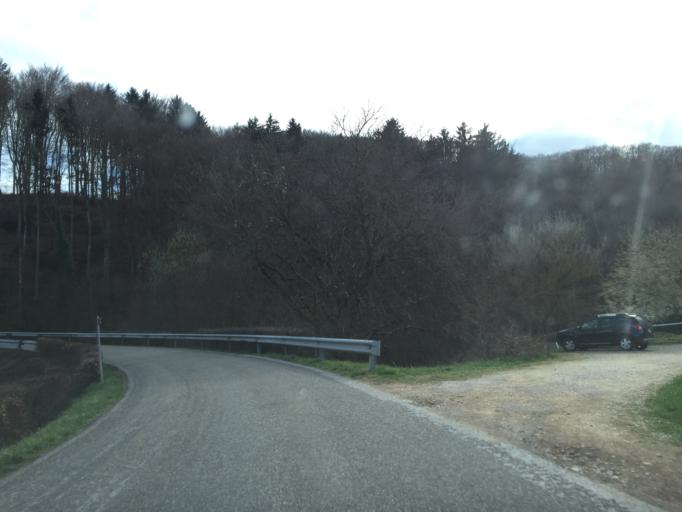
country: CH
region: Vaud
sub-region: Morges District
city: Ferreyres
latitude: 46.6558
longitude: 6.4909
